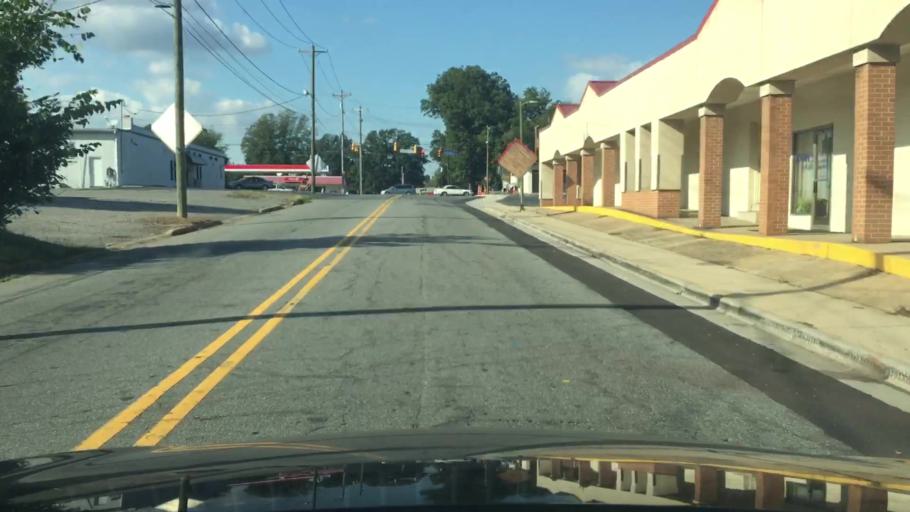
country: US
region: North Carolina
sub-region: Iredell County
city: Mooresville
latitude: 35.5854
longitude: -80.8038
